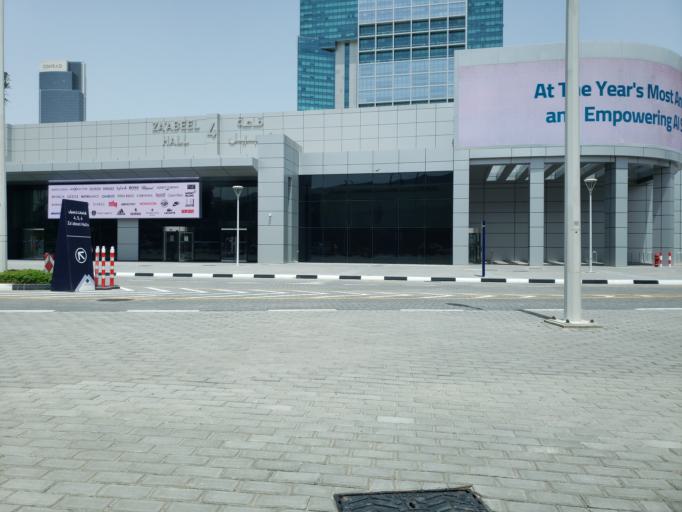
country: AE
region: Ash Shariqah
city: Sharjah
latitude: 25.2251
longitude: 55.2917
